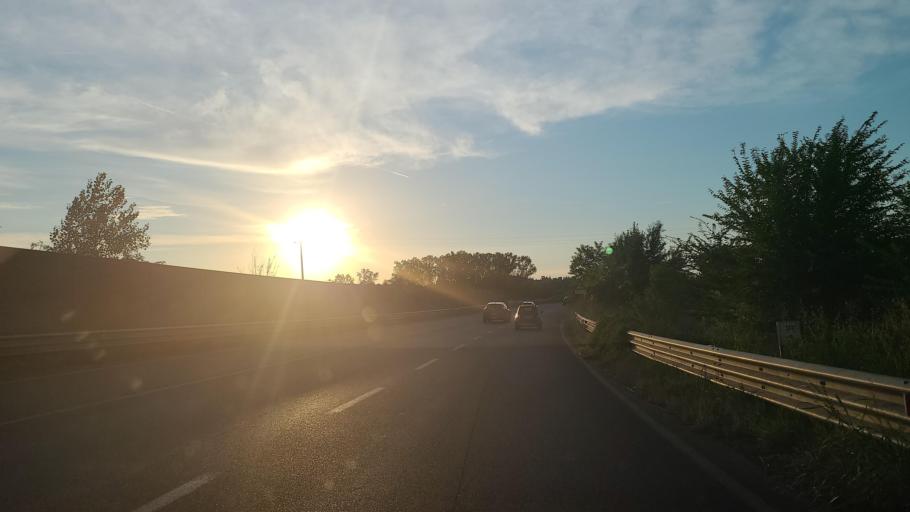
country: IT
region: Tuscany
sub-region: Provincia di Siena
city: Poggibonsi
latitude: 43.4828
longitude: 11.1232
